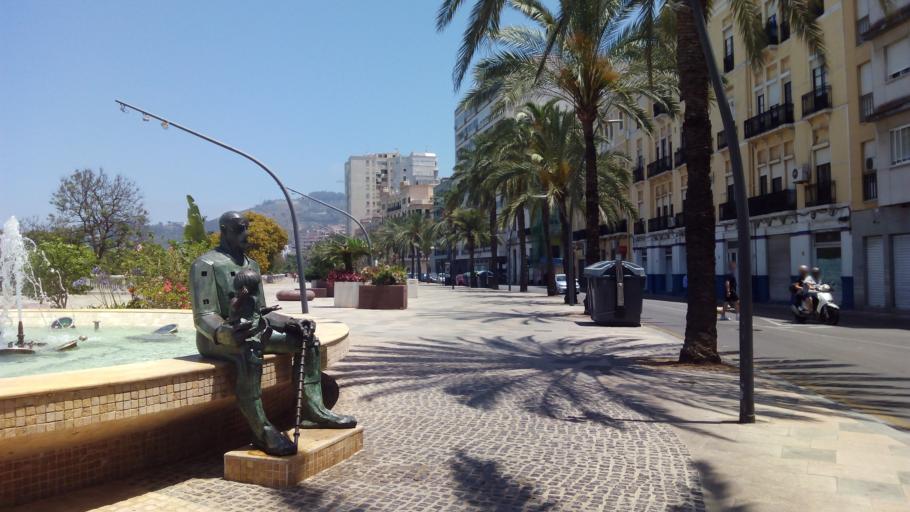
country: ES
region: Ceuta
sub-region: Ceuta
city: Ceuta
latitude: 35.8891
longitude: -5.3105
